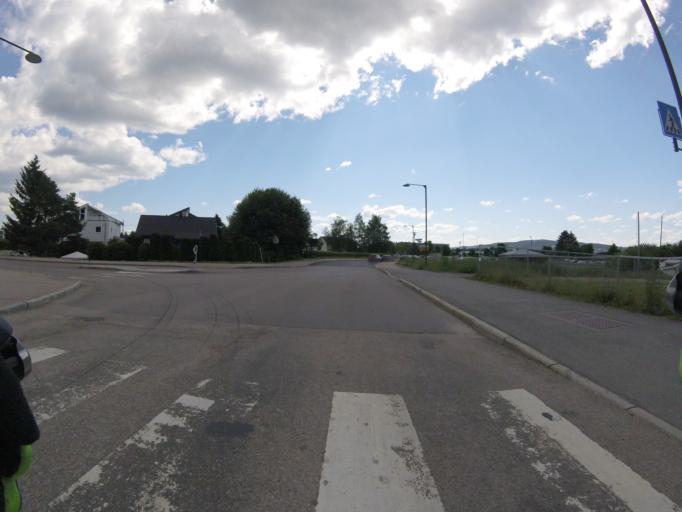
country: NO
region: Akershus
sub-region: Skedsmo
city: Lillestrom
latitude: 59.9735
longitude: 11.0419
